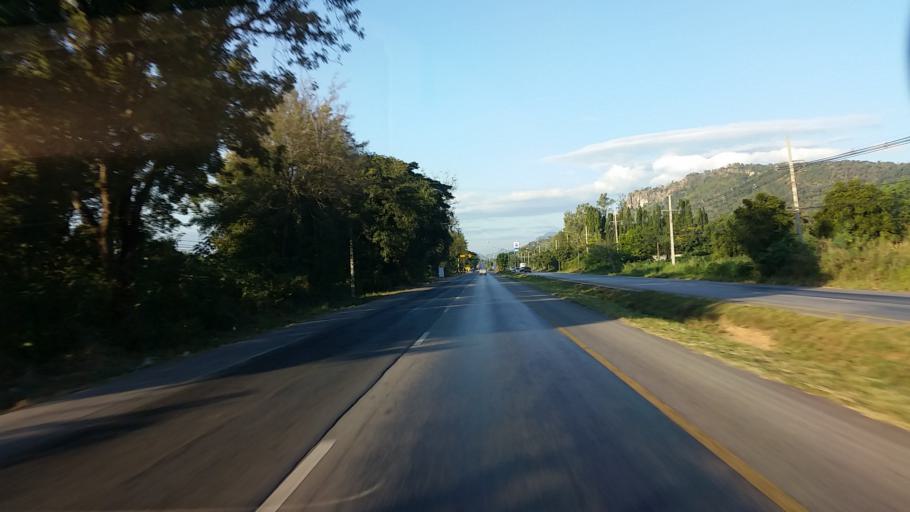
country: TH
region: Lop Buri
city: Chai Badan
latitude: 15.2051
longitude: 101.1010
